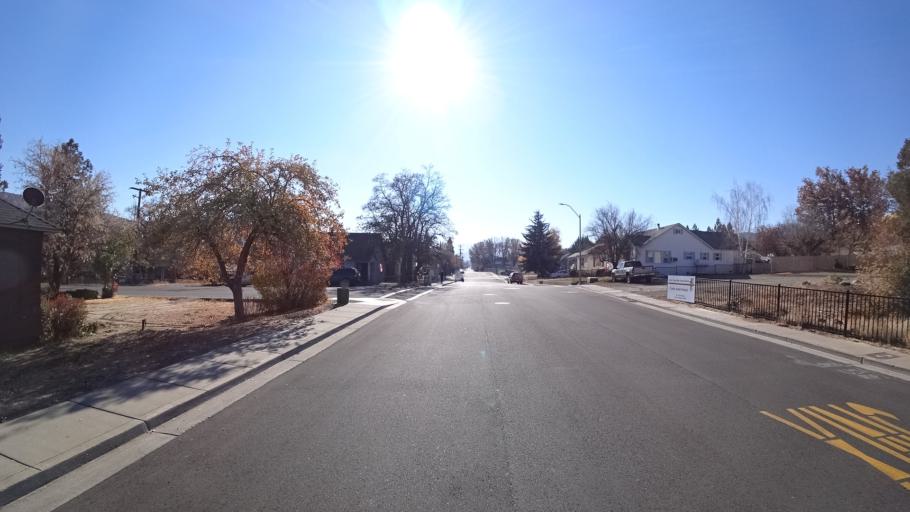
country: US
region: California
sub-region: Siskiyou County
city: Yreka
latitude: 41.7395
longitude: -122.6357
